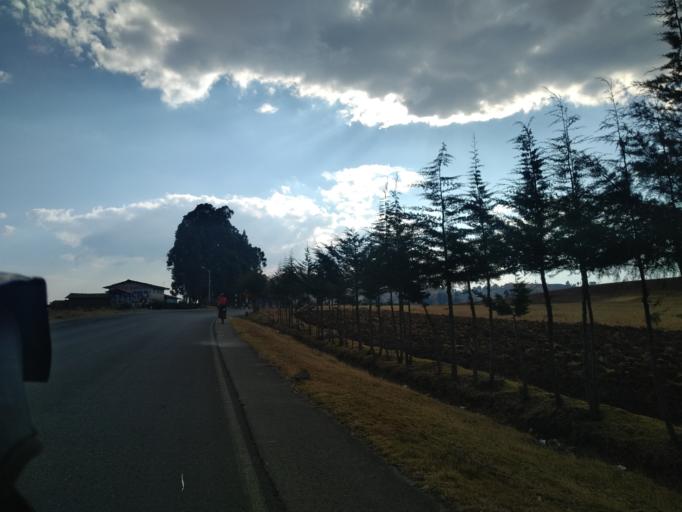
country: PE
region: Cajamarca
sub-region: Provincia de Cajamarca
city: Llacanora
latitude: -7.1468
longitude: -78.3967
